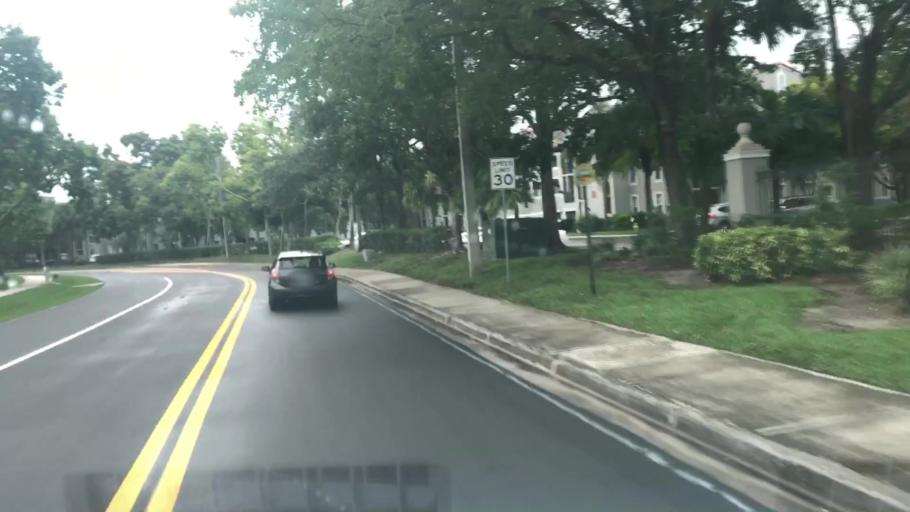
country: US
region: Florida
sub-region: Palm Beach County
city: Boca Pointe
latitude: 26.3003
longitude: -80.1833
